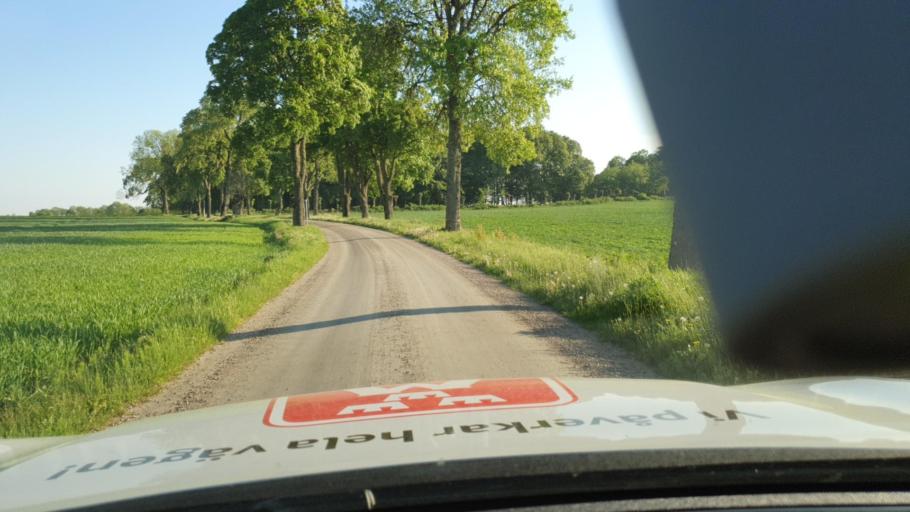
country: SE
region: Vaestra Goetaland
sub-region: Falkopings Kommun
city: Akarp
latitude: 58.1514
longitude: 13.7028
